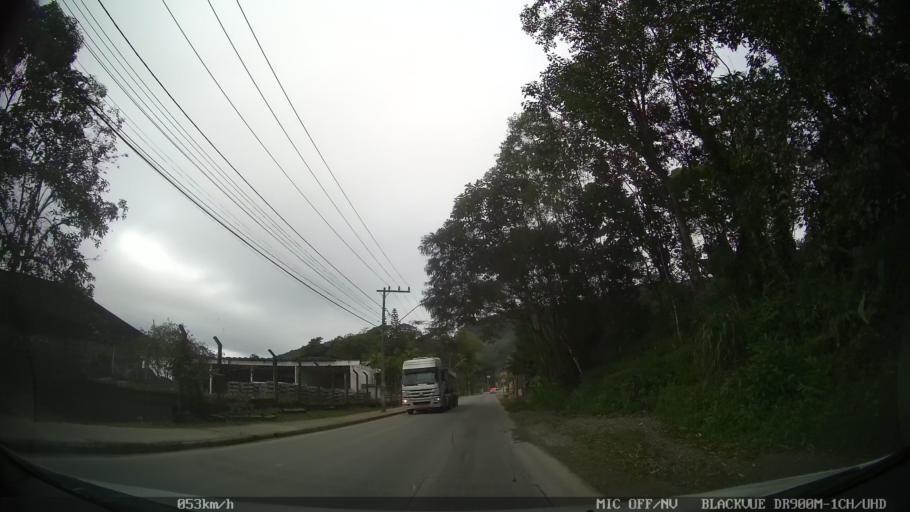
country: BR
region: Santa Catarina
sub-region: Joinville
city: Joinville
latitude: -26.2320
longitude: -48.9206
